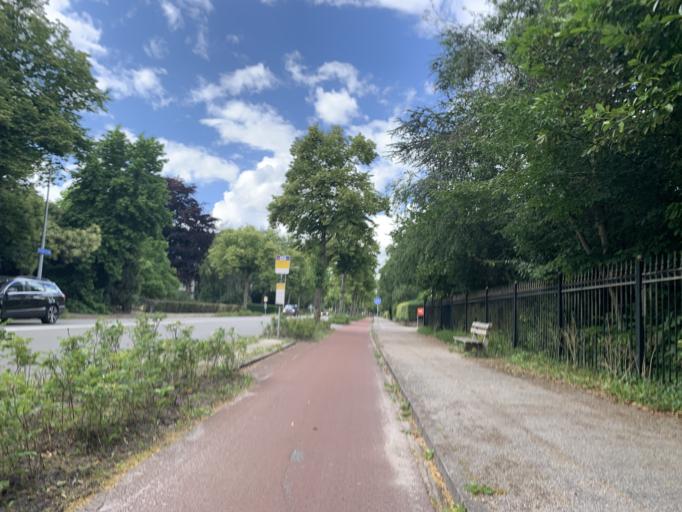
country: NL
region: Groningen
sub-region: Gemeente Haren
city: Haren
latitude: 53.1896
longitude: 6.5849
